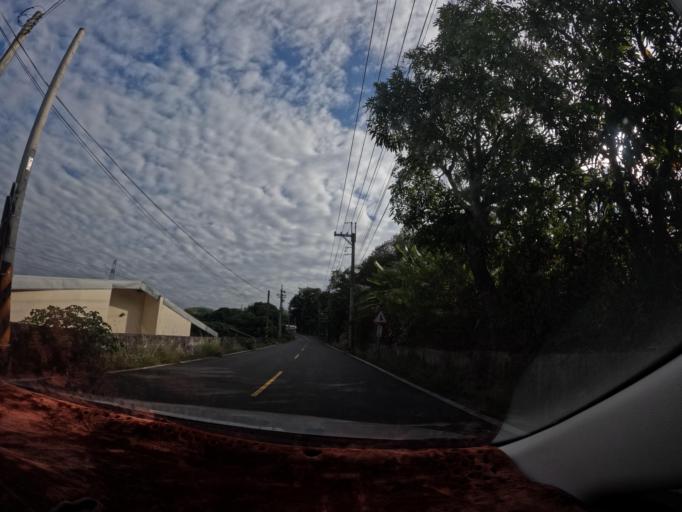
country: TW
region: Taiwan
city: Yujing
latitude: 23.0302
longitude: 120.4146
